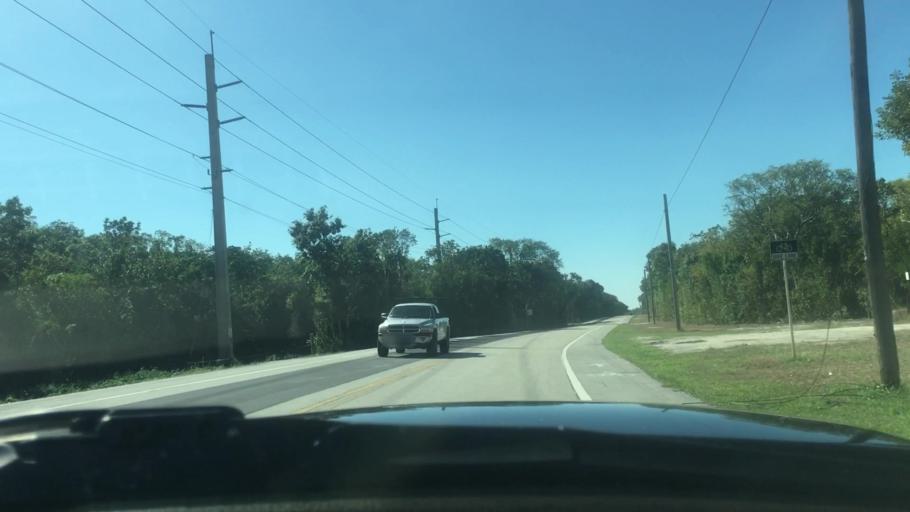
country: US
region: Florida
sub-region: Monroe County
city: North Key Largo
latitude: 25.2276
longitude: -80.3292
